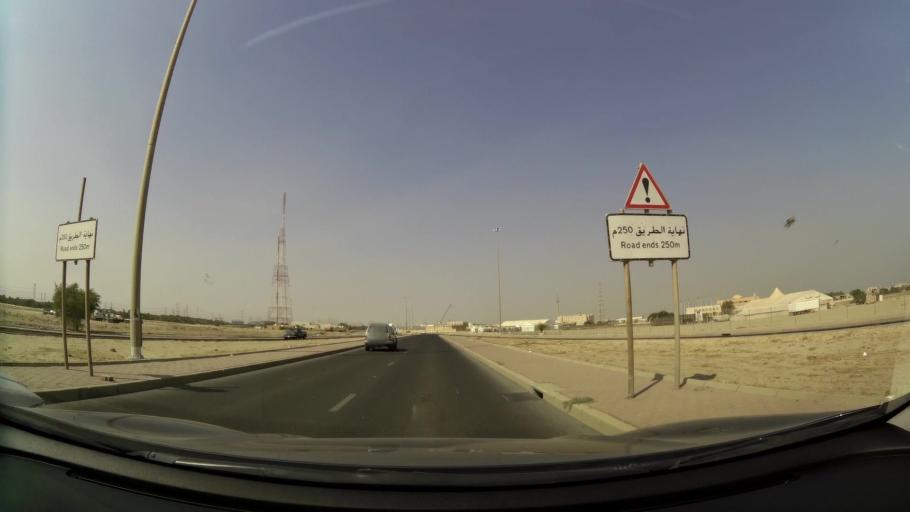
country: KW
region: Al Ahmadi
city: Al Fahahil
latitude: 29.0762
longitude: 48.1085
